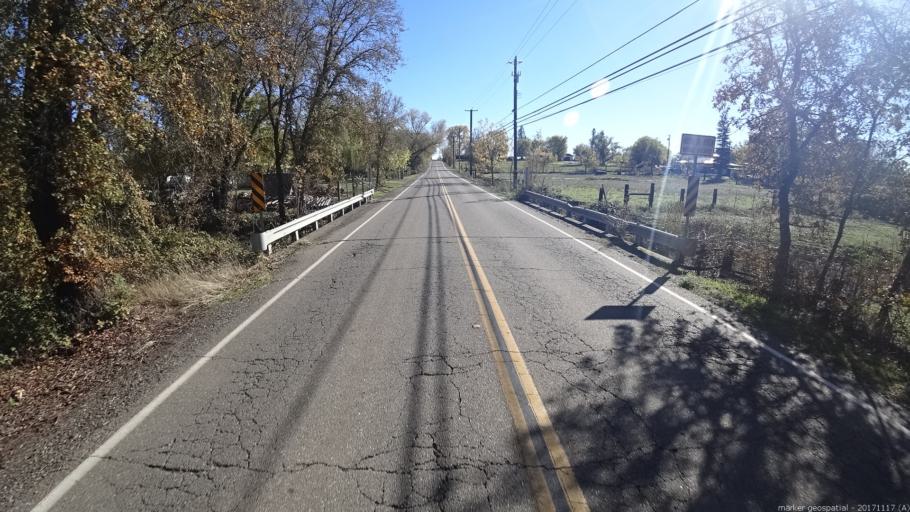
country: US
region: California
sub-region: Shasta County
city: Anderson
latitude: 40.4404
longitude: -122.2454
